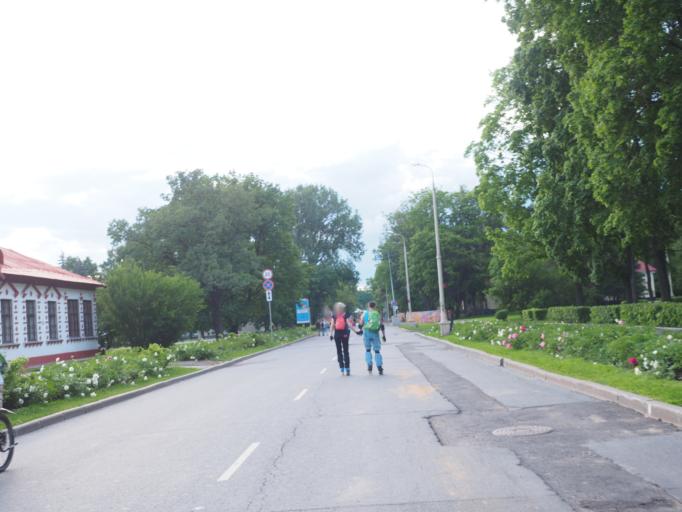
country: RU
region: Moscow
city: Sviblovo
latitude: 55.8352
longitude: 37.6303
